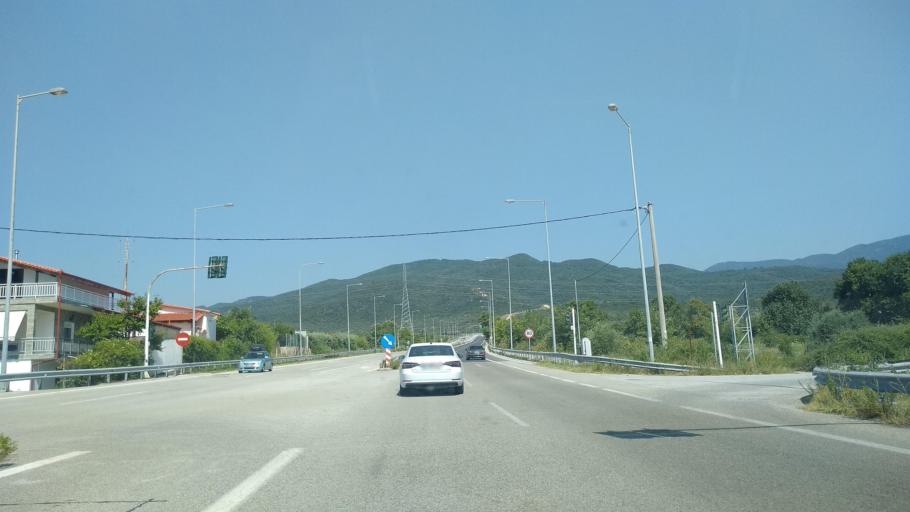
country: GR
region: Central Macedonia
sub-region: Nomos Thessalonikis
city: Nea Vrasna
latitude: 40.7057
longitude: 23.6904
